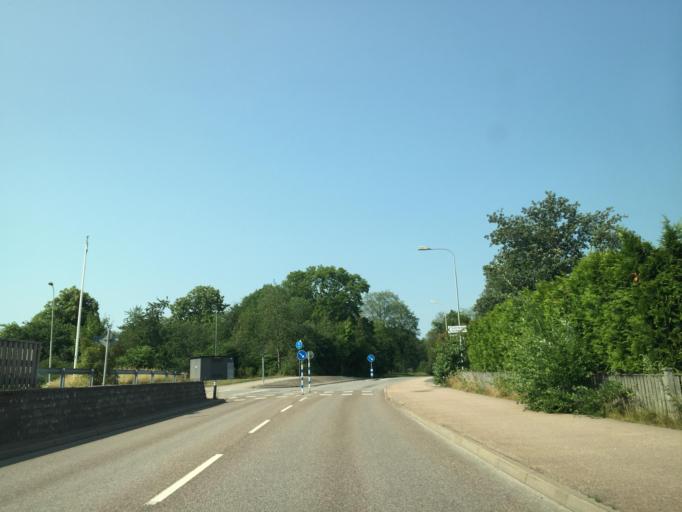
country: SE
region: Vaestra Goetaland
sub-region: Vanersborgs Kommun
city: Vanersborg
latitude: 58.3789
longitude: 12.2939
